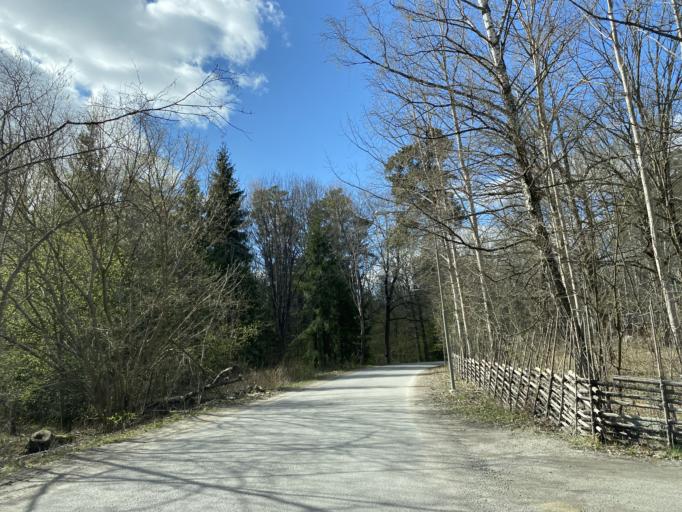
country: SE
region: Stockholm
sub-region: Nacka Kommun
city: Nacka
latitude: 59.3305
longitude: 18.1428
